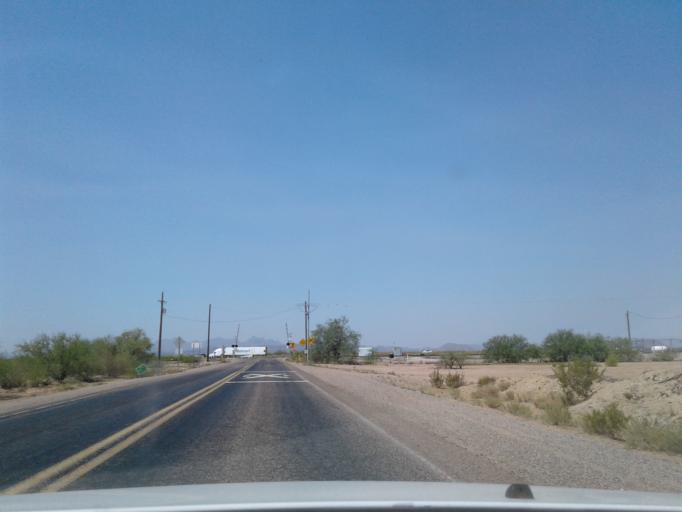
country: US
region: Arizona
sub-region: Pima County
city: Avra Valley
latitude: 32.5931
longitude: -111.3363
